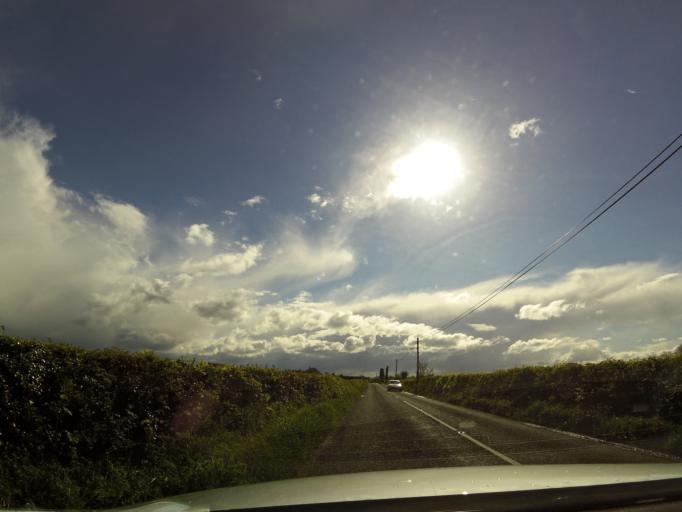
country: IE
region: Munster
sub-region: North Tipperary
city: Templemore
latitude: 52.7973
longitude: -7.8059
